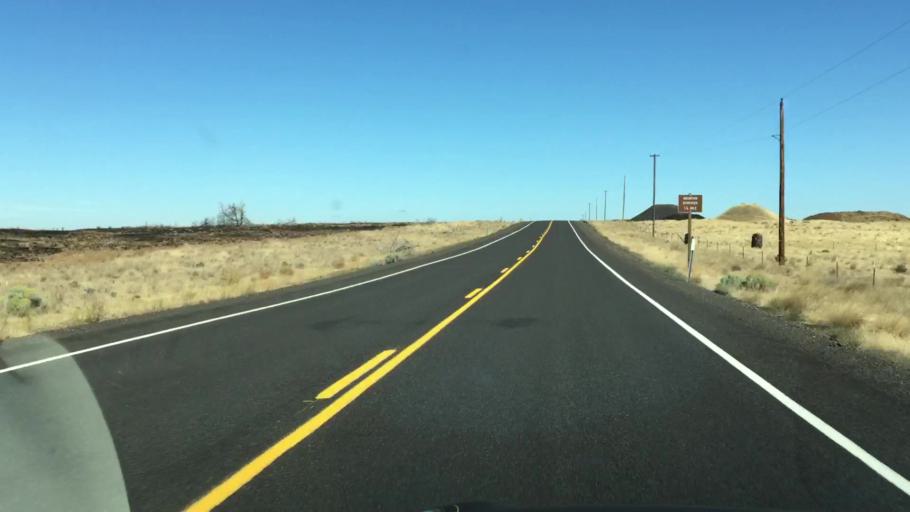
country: US
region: Oregon
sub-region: Jefferson County
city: Warm Springs
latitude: 44.9784
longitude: -120.9891
